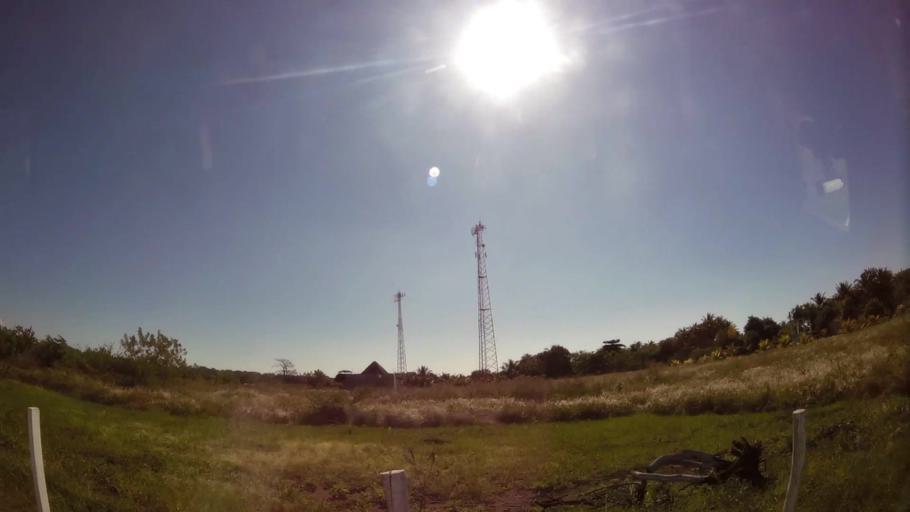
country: GT
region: Santa Rosa
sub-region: Municipio de Taxisco
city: Taxisco
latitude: 13.8686
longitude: -90.4151
